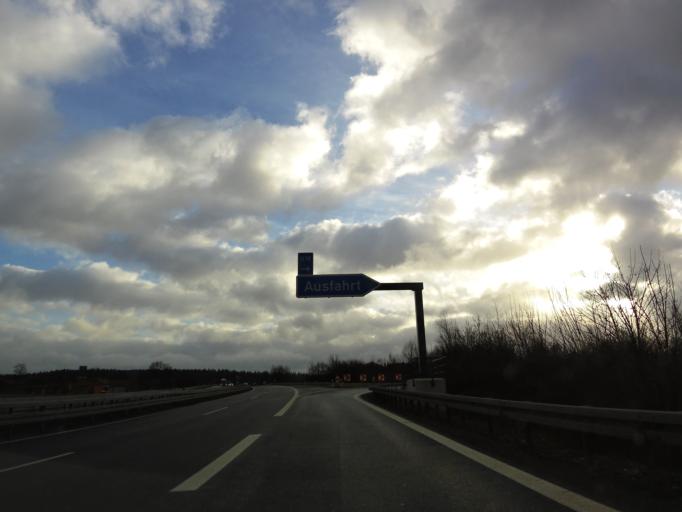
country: DE
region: Bavaria
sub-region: Upper Franconia
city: Thiersheim
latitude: 50.0766
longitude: 12.1015
